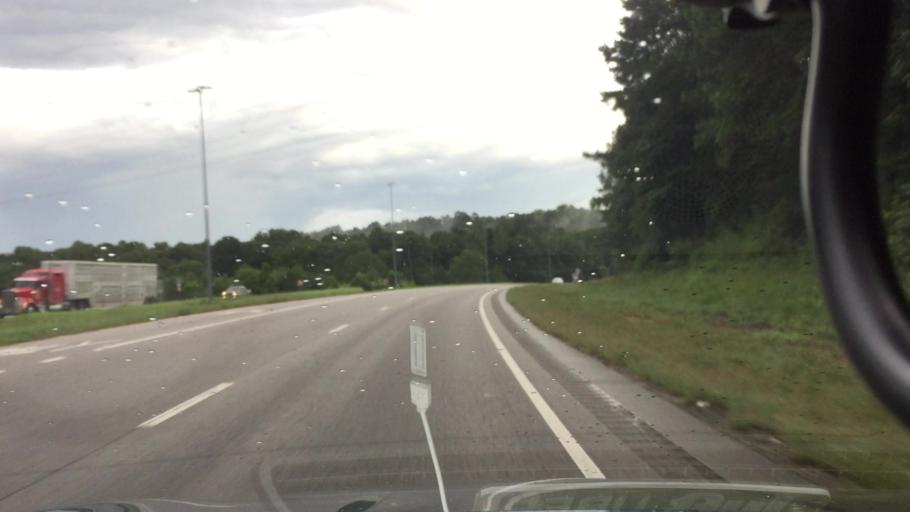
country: US
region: Alabama
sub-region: Pike County
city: Troy
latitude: 31.8336
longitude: -85.9911
